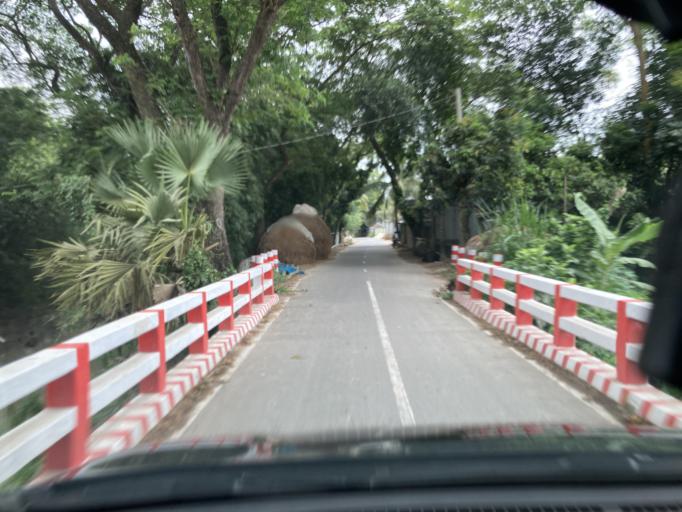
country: BD
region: Dhaka
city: Dohar
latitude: 23.7743
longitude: 90.0664
